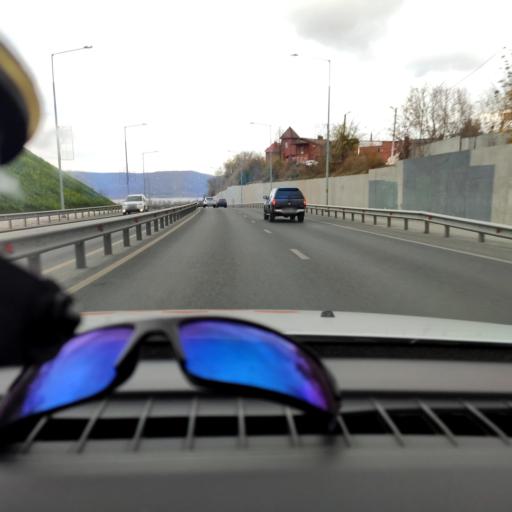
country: RU
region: Samara
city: Volzhskiy
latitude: 53.3704
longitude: 50.1877
